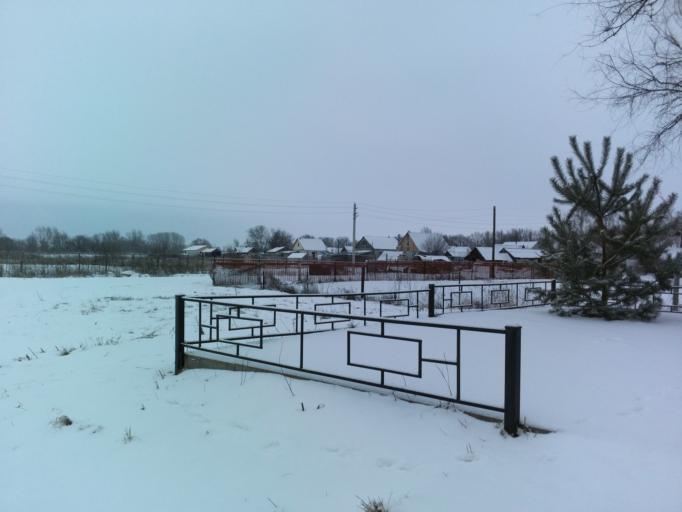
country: RU
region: Voronezj
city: Boguchar
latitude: 49.9357
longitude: 40.5749
